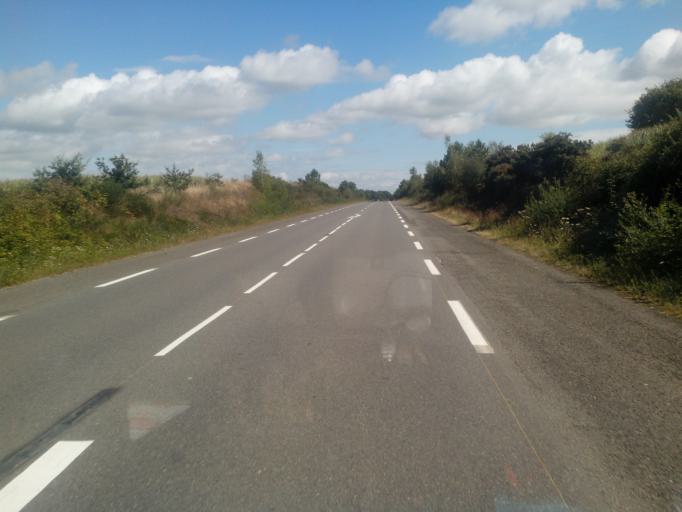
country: FR
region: Brittany
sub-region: Departement du Morbihan
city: Limerzel
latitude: 47.6153
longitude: -2.3983
